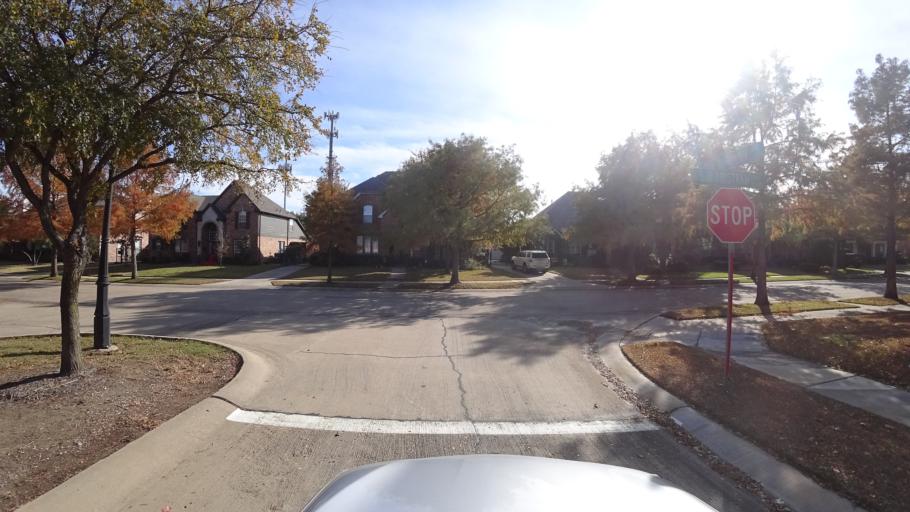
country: US
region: Texas
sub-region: Denton County
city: The Colony
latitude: 33.0278
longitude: -96.8954
